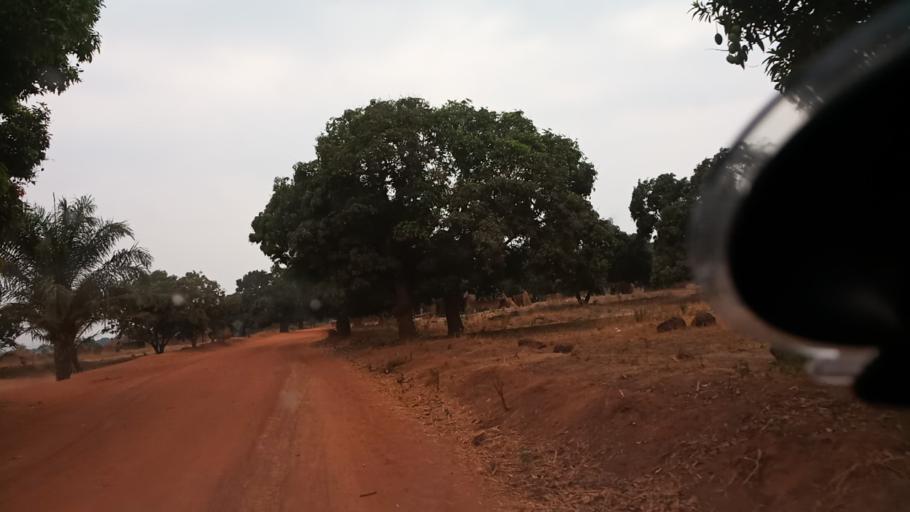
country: ZM
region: Luapula
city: Nchelenge
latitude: -9.1873
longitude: 28.2821
